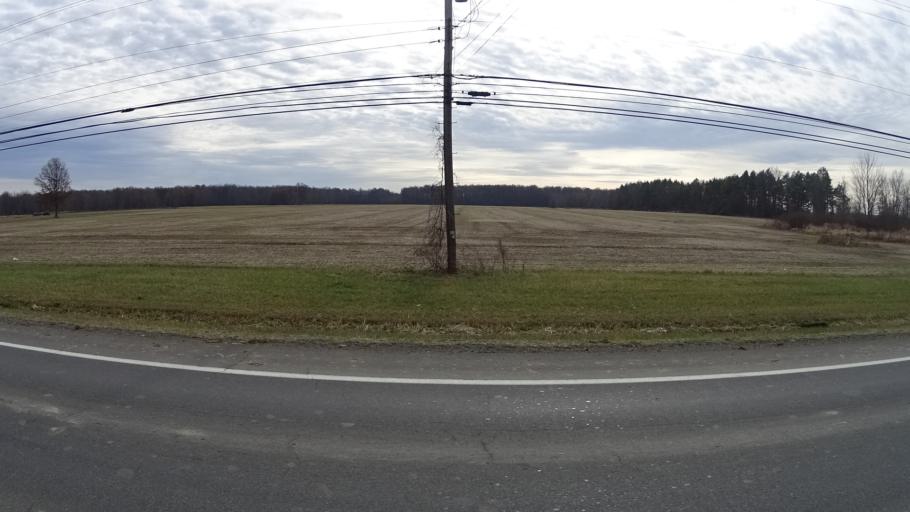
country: US
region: Ohio
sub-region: Lorain County
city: Eaton Estates
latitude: 41.3133
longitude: -81.9692
